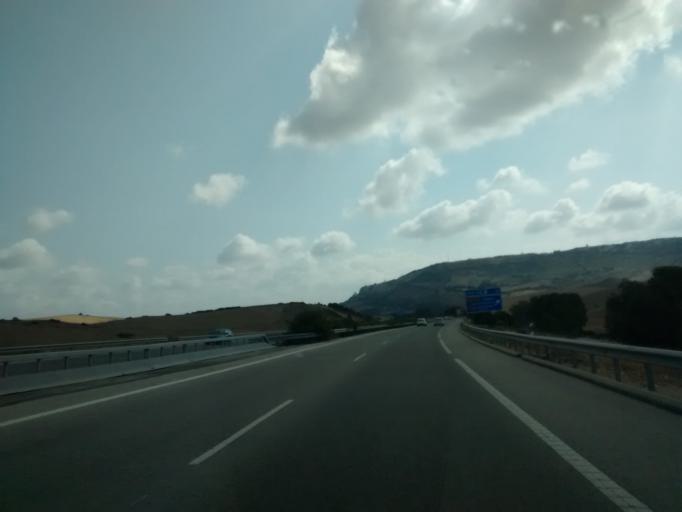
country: ES
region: Andalusia
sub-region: Provincia de Cadiz
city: Vejer de la Frontera
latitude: 36.2524
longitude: -5.9996
